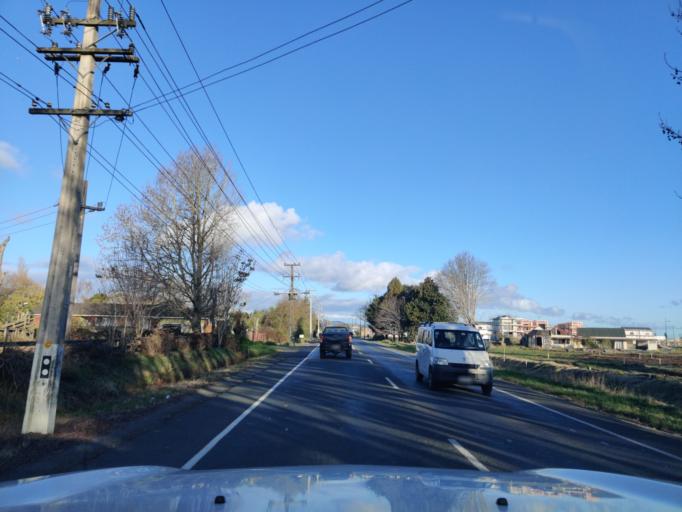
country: NZ
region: Auckland
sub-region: Auckland
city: Red Hill
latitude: -37.0463
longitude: 174.9541
